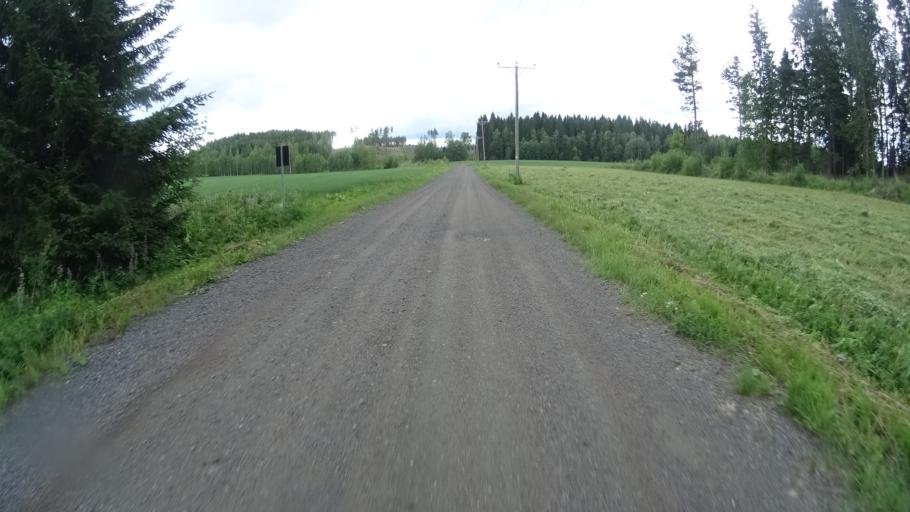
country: FI
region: Uusimaa
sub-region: Helsinki
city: Karkkila
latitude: 60.5862
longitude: 24.1654
